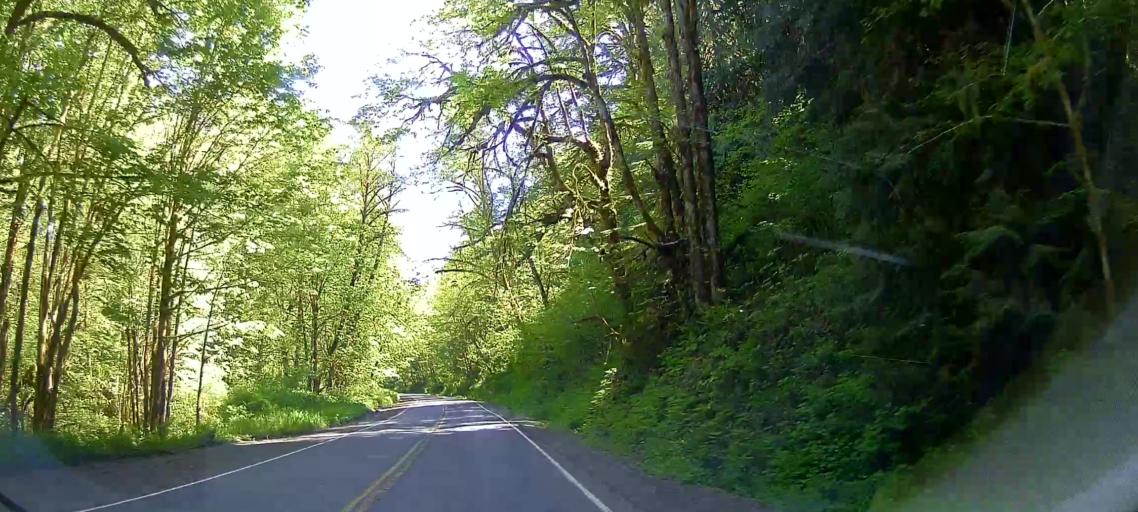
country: US
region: Washington
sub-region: Snohomish County
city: Darrington
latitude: 48.5016
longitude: -121.7105
